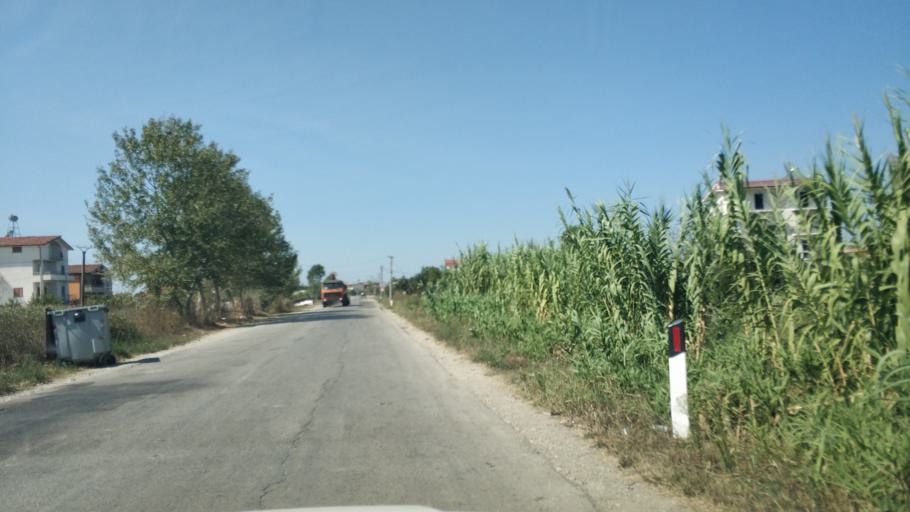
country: AL
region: Fier
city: Terbuf
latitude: 41.0520
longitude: 19.5864
